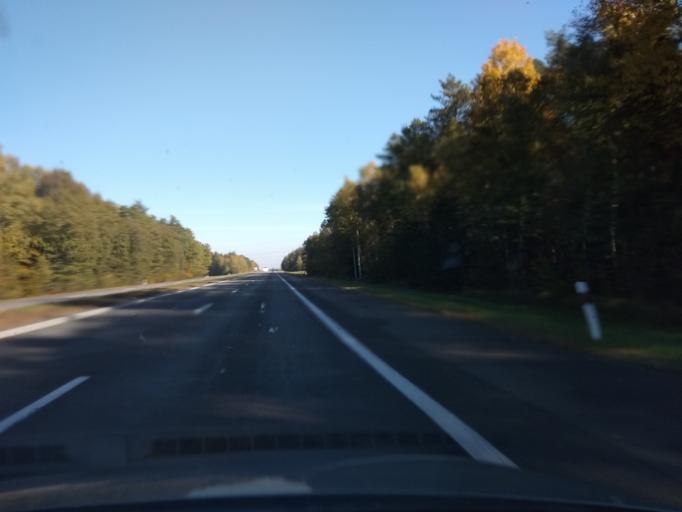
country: BY
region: Brest
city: Nyakhachava
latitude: 52.6531
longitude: 25.2589
